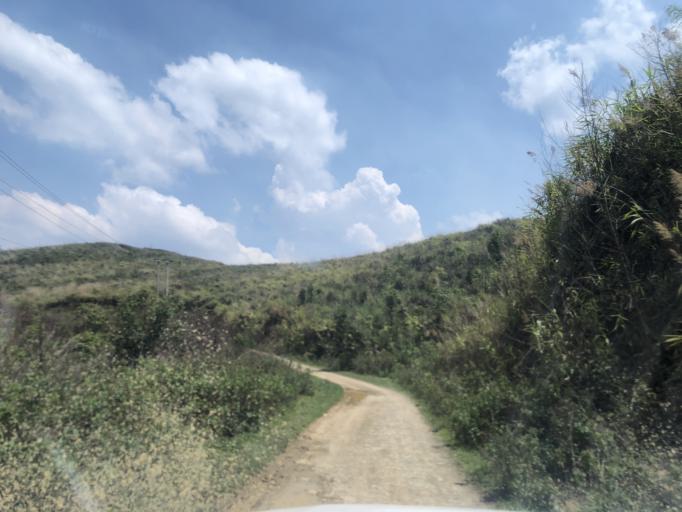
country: LA
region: Phongsali
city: Phongsali
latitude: 21.4037
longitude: 102.1861
